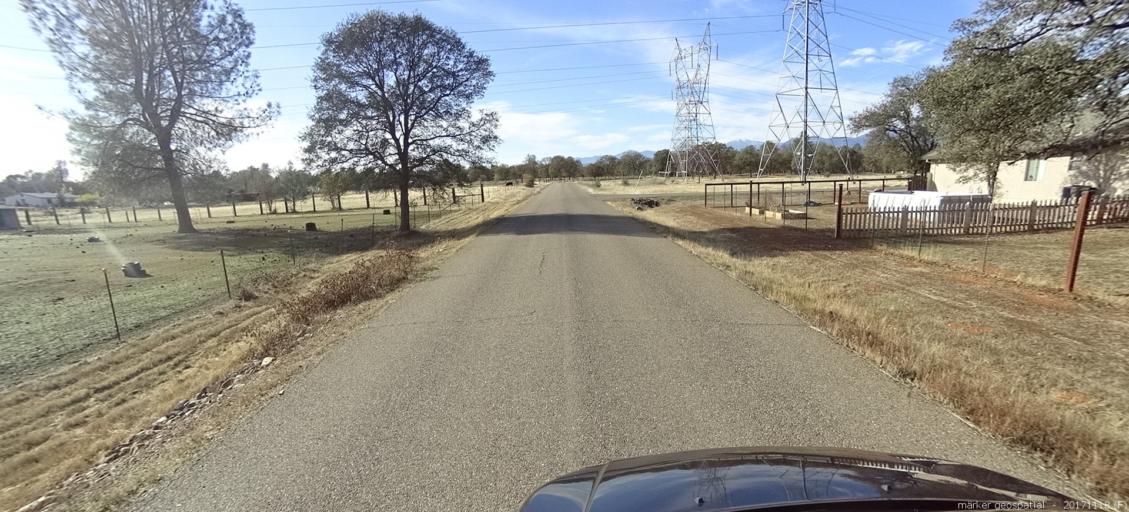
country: US
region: California
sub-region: Shasta County
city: Redding
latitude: 40.4726
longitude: -122.4243
